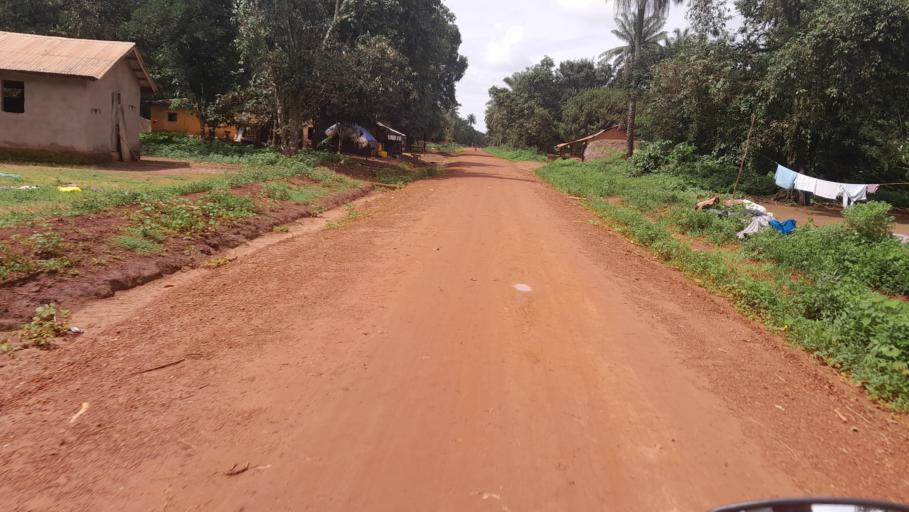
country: GN
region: Boke
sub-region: Boffa
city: Boffa
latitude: 10.0159
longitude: -13.8884
